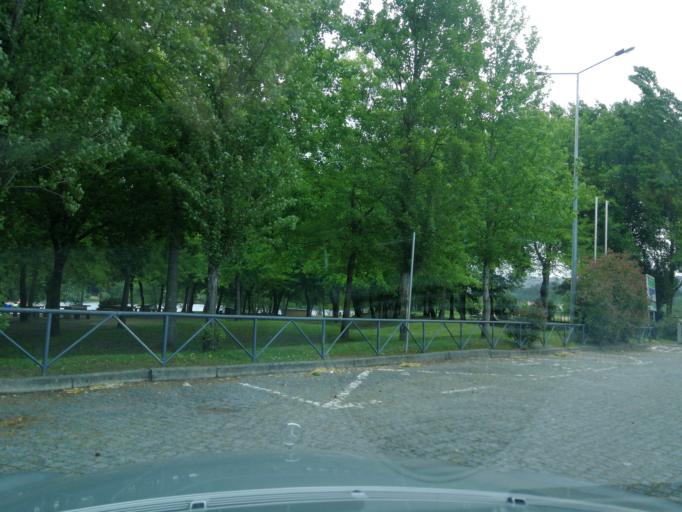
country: PT
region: Braga
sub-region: Braga
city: Adaufe
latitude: 41.6093
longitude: -8.4070
